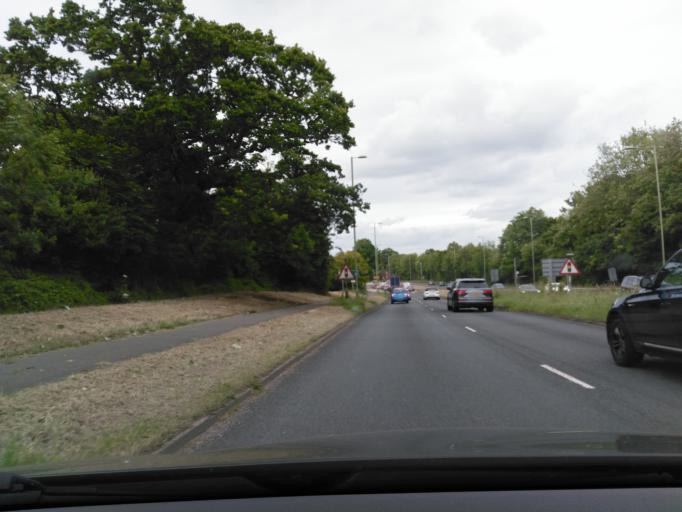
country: GB
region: England
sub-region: Hampshire
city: Basingstoke
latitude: 51.2797
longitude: -1.0734
